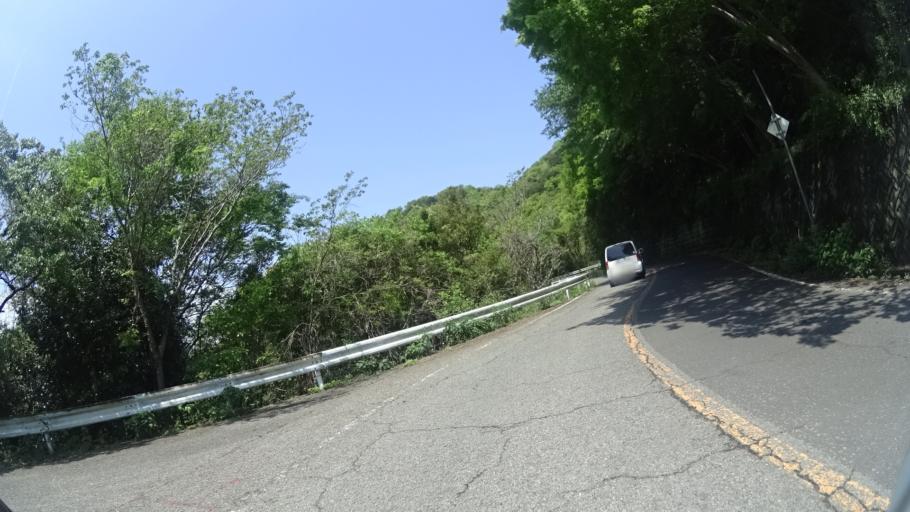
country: JP
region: Tokushima
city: Tokushima-shi
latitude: 34.0650
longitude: 134.5366
